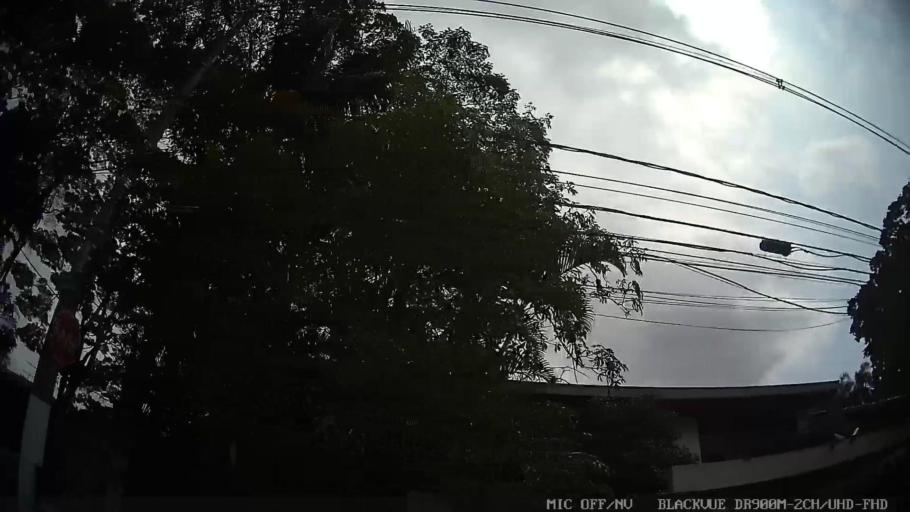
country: BR
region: Sao Paulo
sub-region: Diadema
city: Diadema
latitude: -23.6330
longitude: -46.6750
